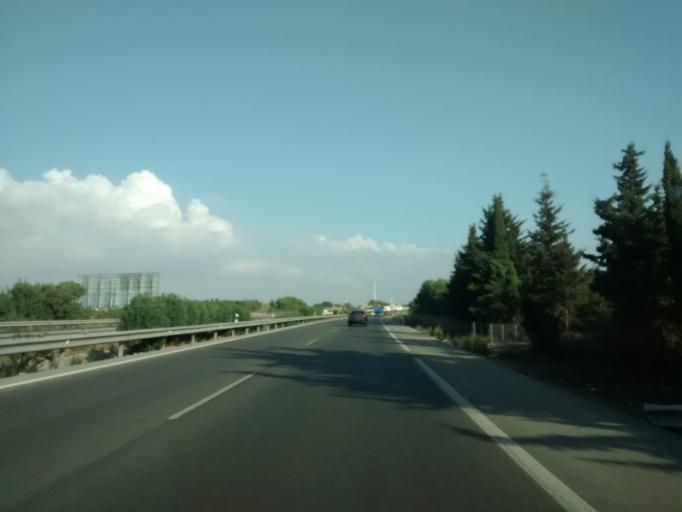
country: ES
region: Andalusia
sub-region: Provincia de Cadiz
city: Chiclana de la Frontera
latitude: 36.4418
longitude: -6.1318
